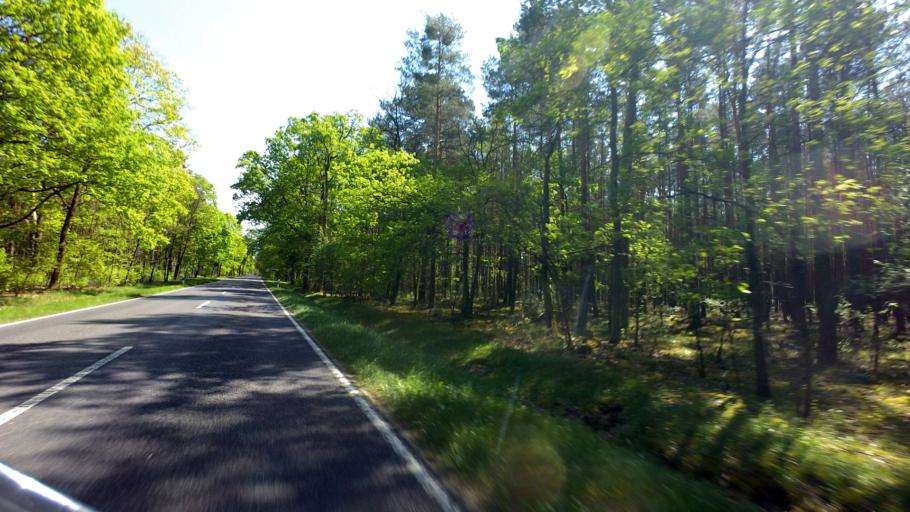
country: DE
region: Brandenburg
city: Munchehofe
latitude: 52.0998
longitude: 13.8229
